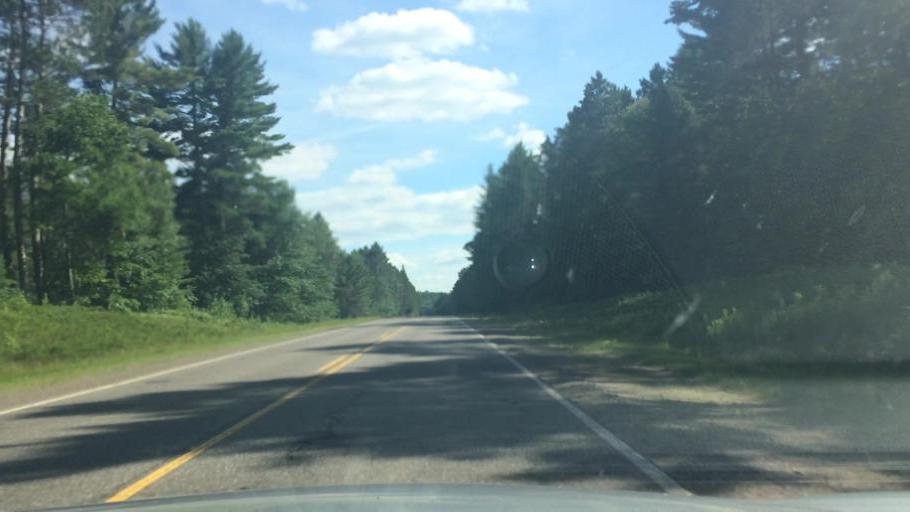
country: US
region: Wisconsin
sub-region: Vilas County
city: Lac du Flambeau
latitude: 46.0541
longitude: -89.6498
